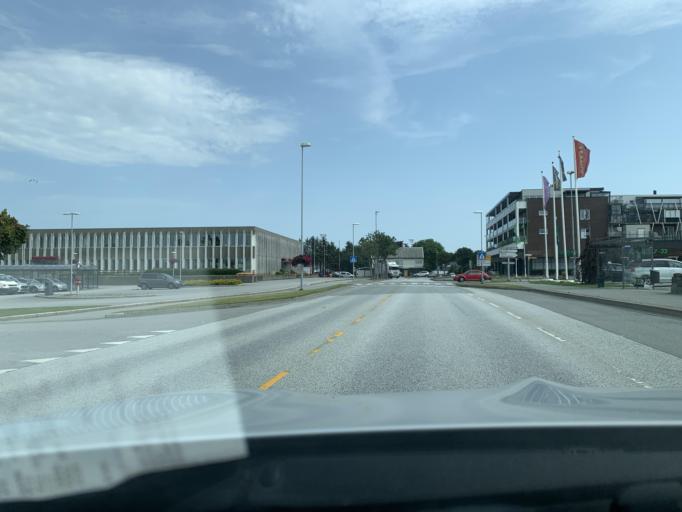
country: NO
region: Rogaland
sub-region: Klepp
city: Kleppe
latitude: 58.7769
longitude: 5.6281
